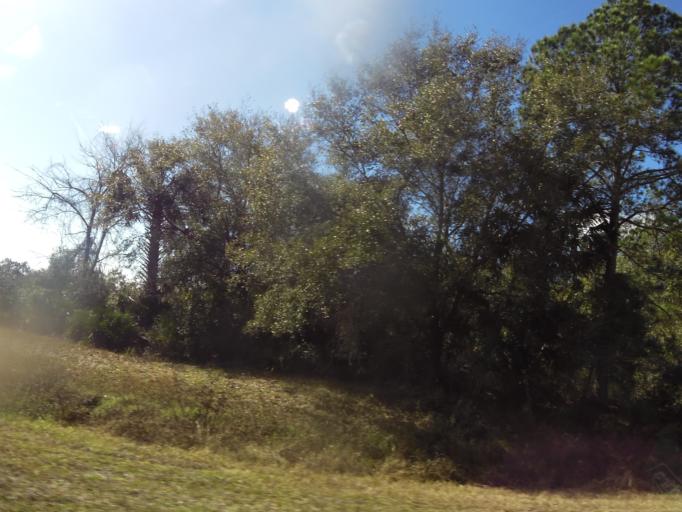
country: US
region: Florida
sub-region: Volusia County
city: Pierson
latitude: 29.2534
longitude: -81.4678
